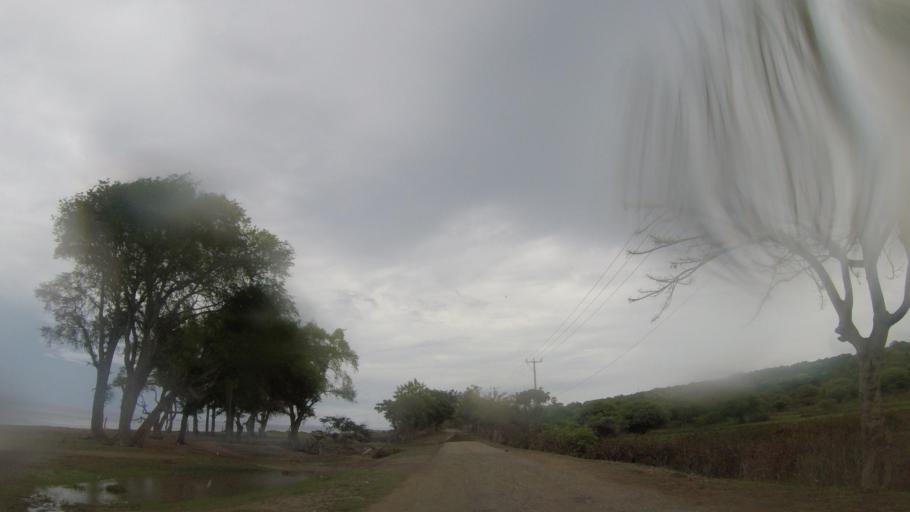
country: TL
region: Lautem
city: Lospalos
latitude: -8.3500
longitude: 126.9203
